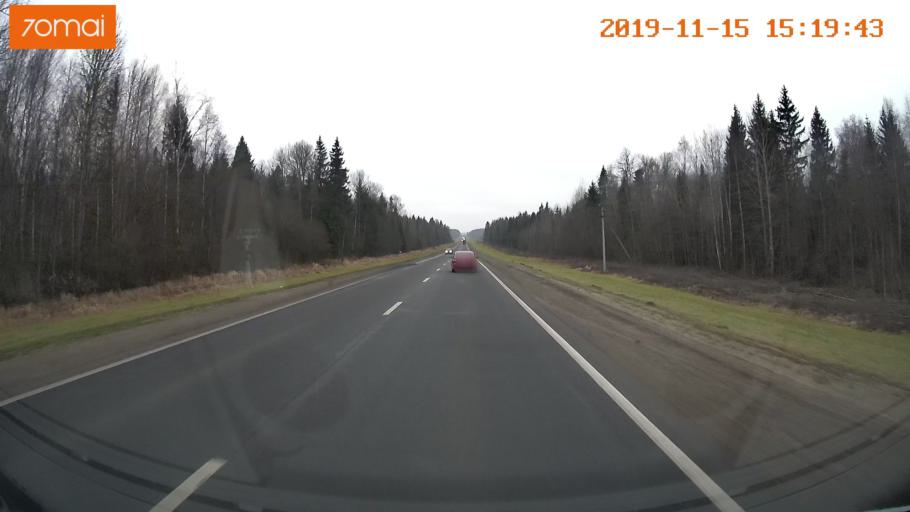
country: RU
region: Jaroslavl
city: Danilov
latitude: 58.2313
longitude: 40.1732
